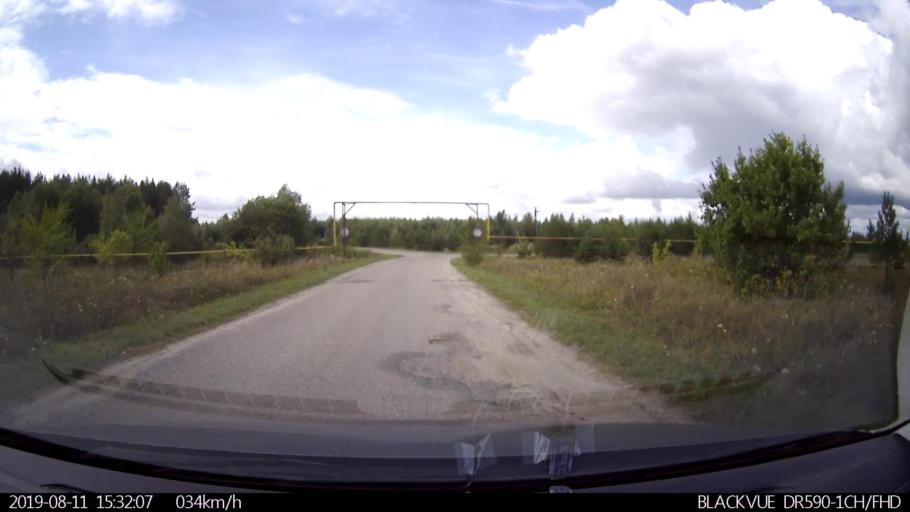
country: RU
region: Ulyanovsk
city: Ignatovka
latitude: 53.8592
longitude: 47.5758
